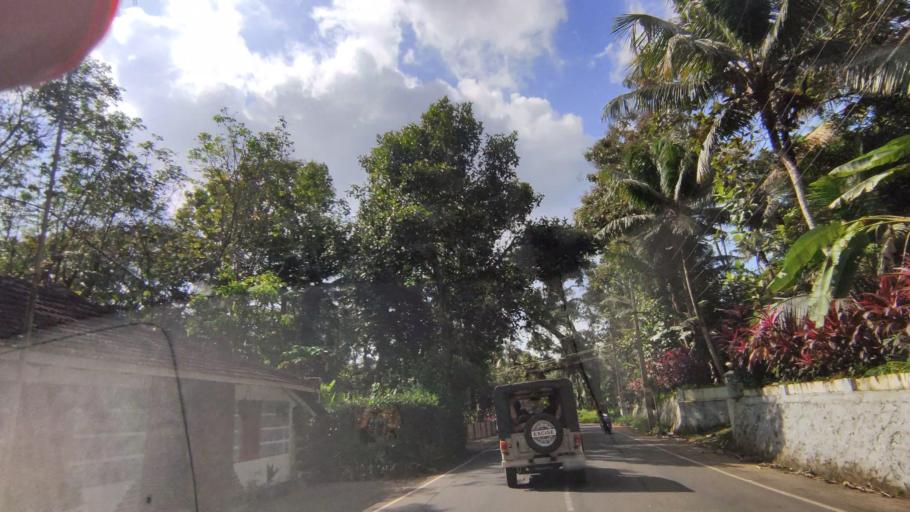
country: IN
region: Kerala
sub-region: Kottayam
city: Kottayam
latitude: 9.6744
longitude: 76.5285
